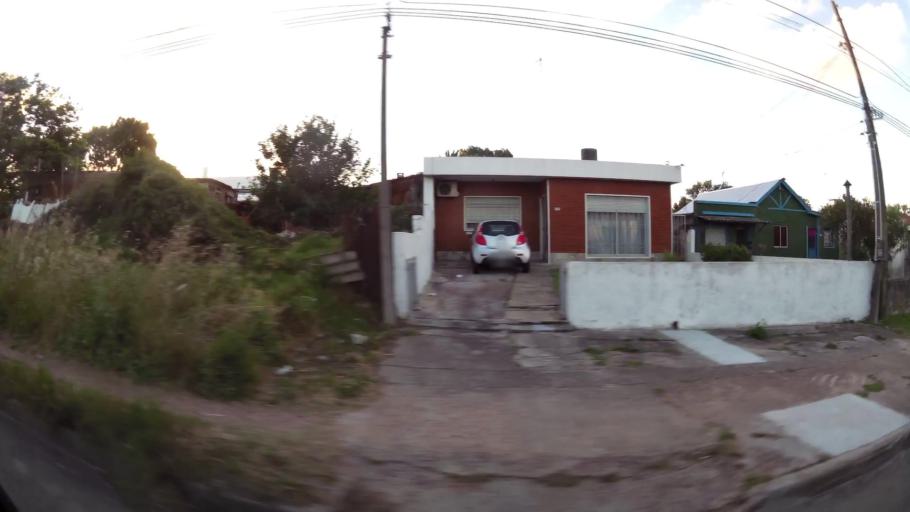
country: UY
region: Montevideo
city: Montevideo
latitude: -34.8853
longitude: -56.1206
